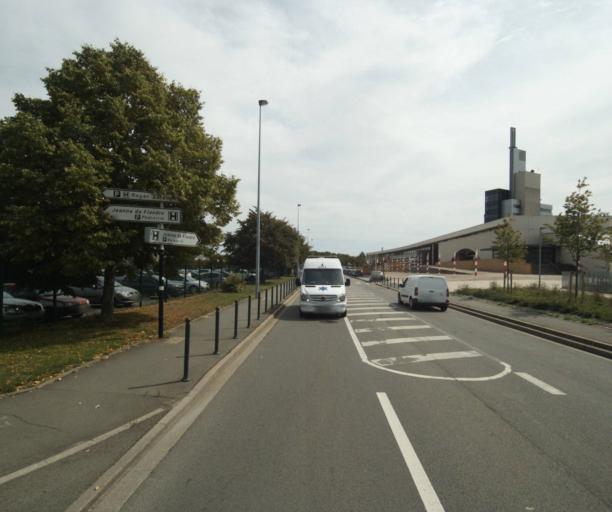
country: FR
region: Nord-Pas-de-Calais
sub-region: Departement du Nord
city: Loos
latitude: 50.6050
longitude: 3.0305
